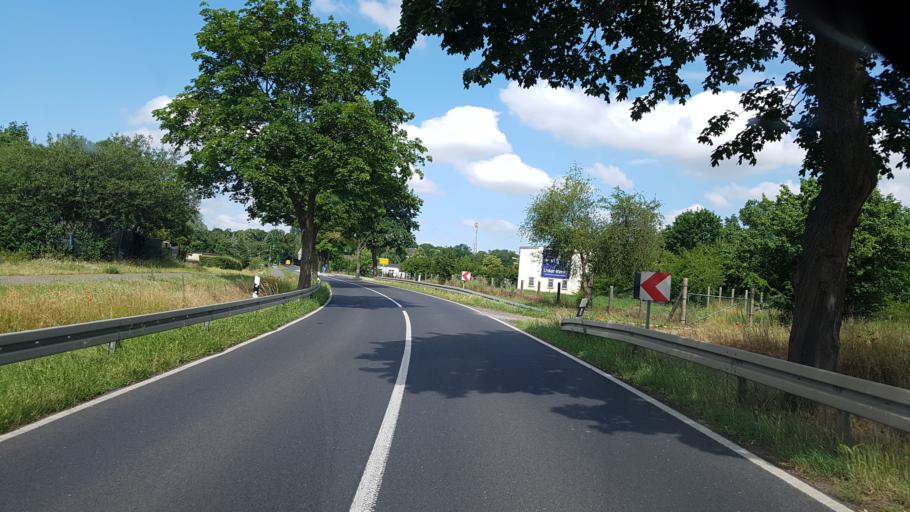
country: DE
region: Brandenburg
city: Prenzlau
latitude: 53.3620
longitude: 13.8109
